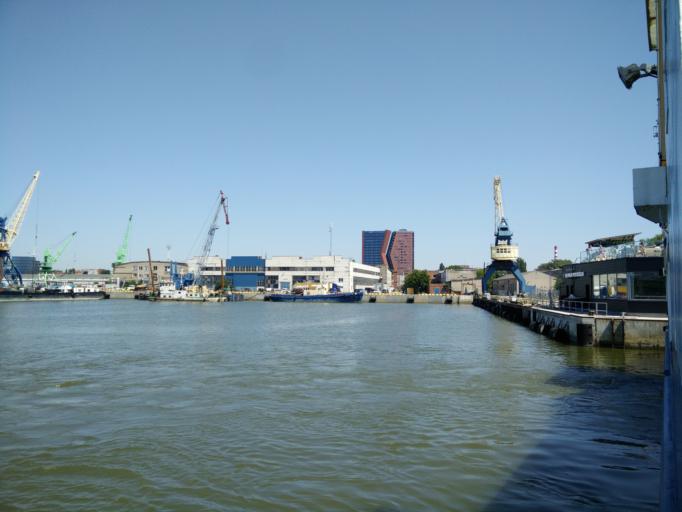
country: LT
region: Klaipedos apskritis
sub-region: Klaipeda
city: Klaipeda
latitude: 55.7064
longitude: 21.1222
